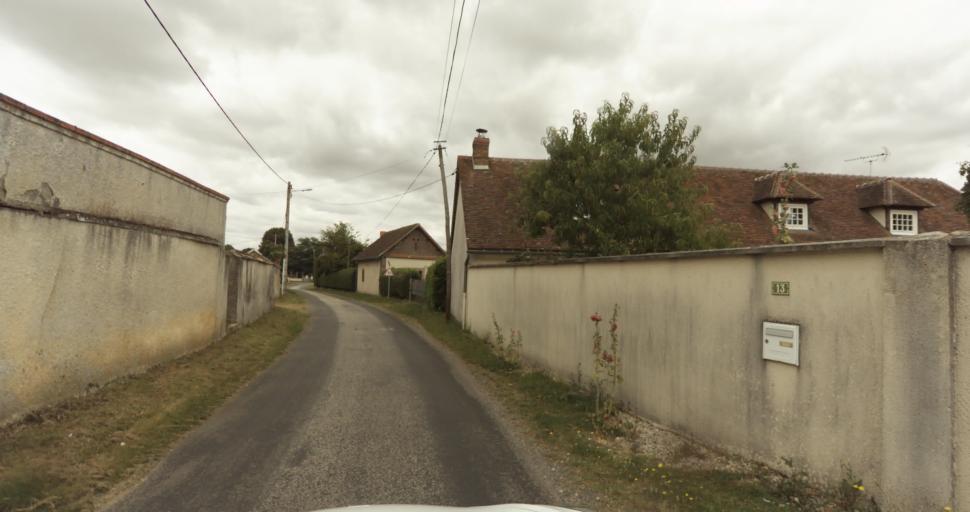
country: FR
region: Haute-Normandie
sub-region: Departement de l'Eure
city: Nonancourt
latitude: 48.7965
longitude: 1.1321
